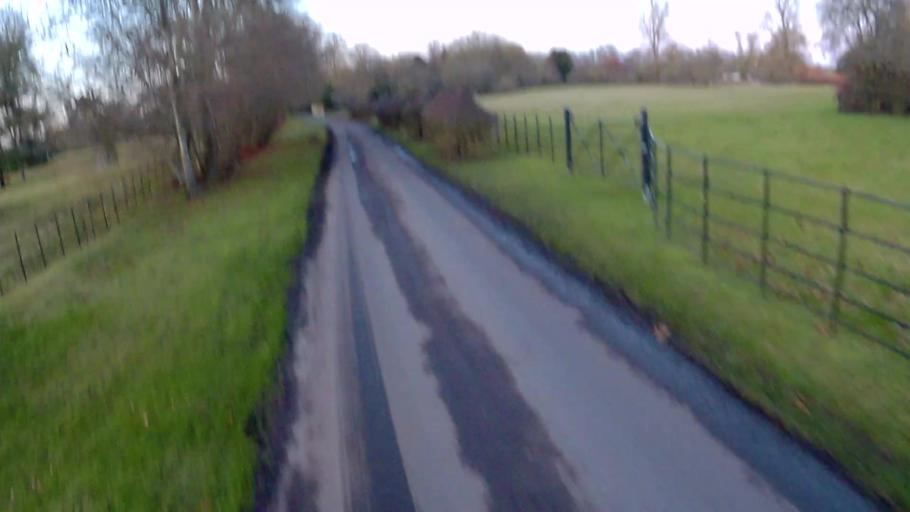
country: GB
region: England
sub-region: Hampshire
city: Overton
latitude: 51.2468
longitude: -1.2172
